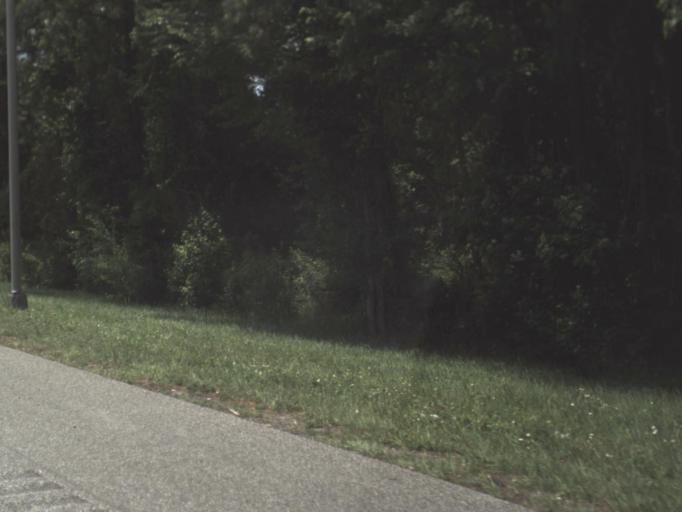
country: US
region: Florida
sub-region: Saint Johns County
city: Fruit Cove
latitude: 30.1688
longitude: -81.5944
